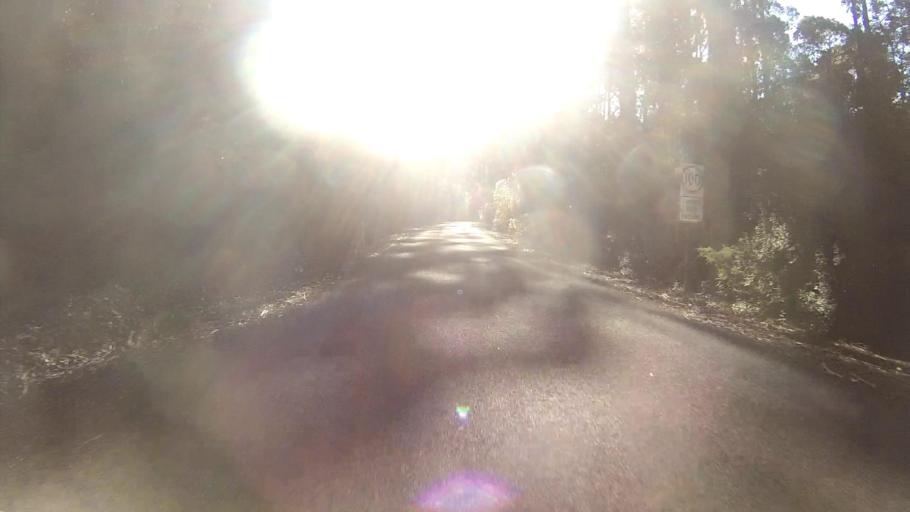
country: AU
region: Tasmania
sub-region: Sorell
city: Sorell
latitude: -43.0057
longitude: 147.9325
